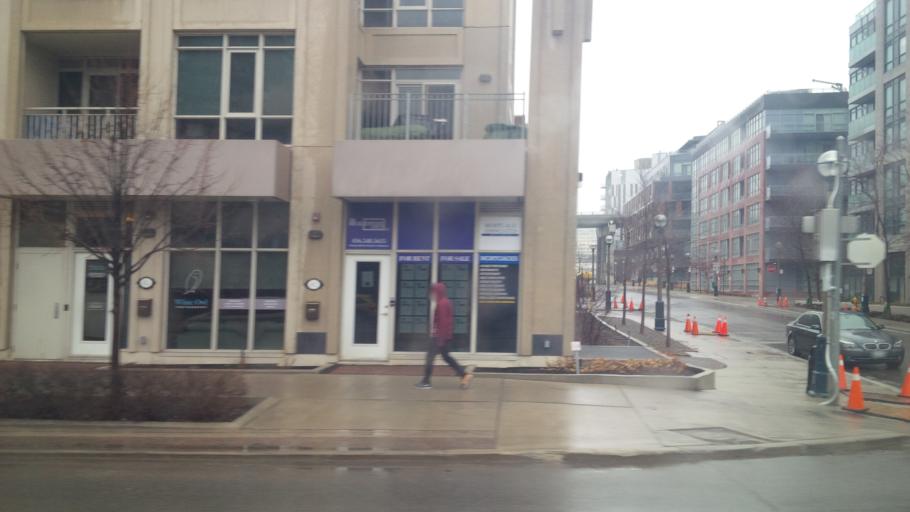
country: CA
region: Ontario
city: Toronto
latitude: 43.6362
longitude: -79.4013
